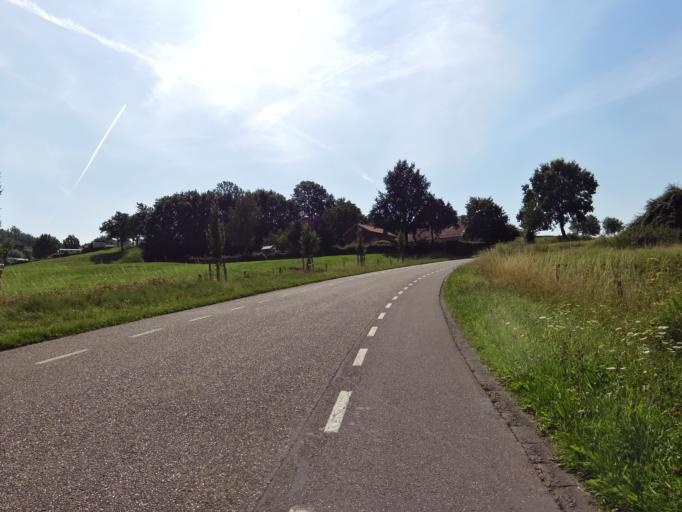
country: BE
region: Wallonia
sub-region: Province de Liege
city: Plombieres
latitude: 50.7718
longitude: 5.9258
